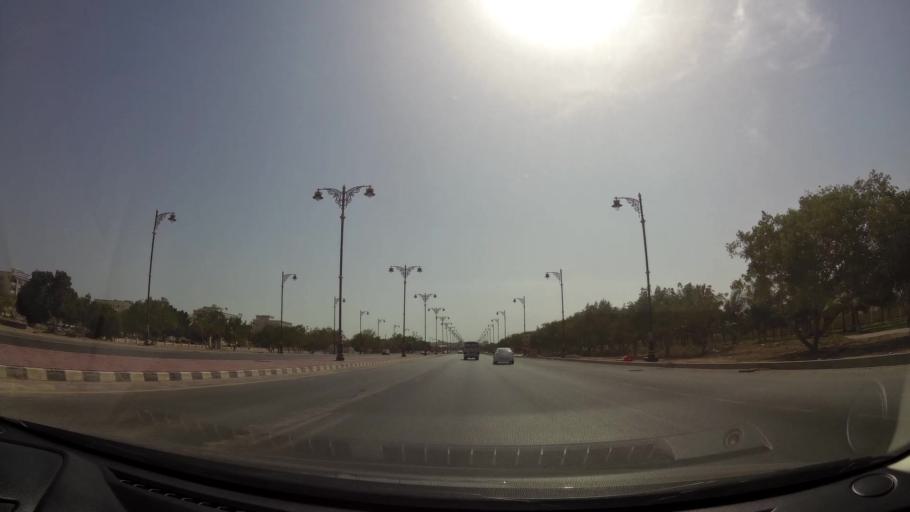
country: OM
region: Zufar
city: Salalah
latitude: 17.0233
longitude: 54.0784
